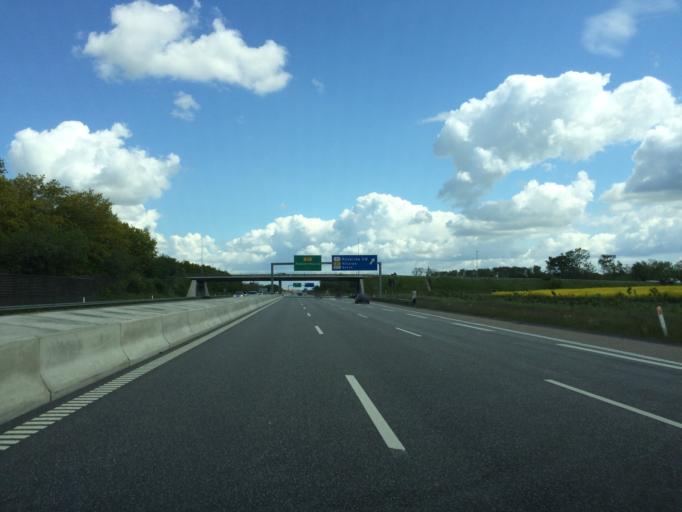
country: DK
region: Zealand
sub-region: Roskilde Kommune
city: Vindinge
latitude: 55.6319
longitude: 12.1125
